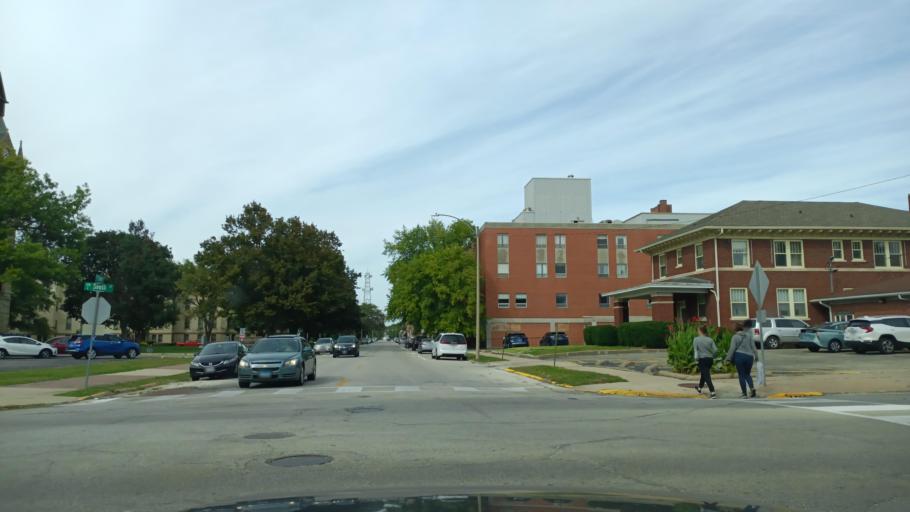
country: US
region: Illinois
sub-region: Knox County
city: Galesburg
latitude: 40.9437
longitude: -90.3697
